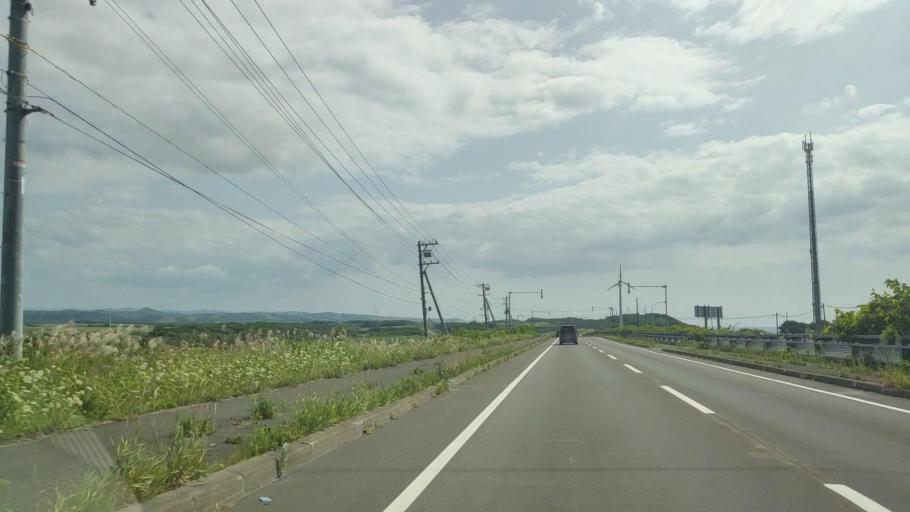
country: JP
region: Hokkaido
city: Rumoi
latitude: 44.3022
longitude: 141.6531
